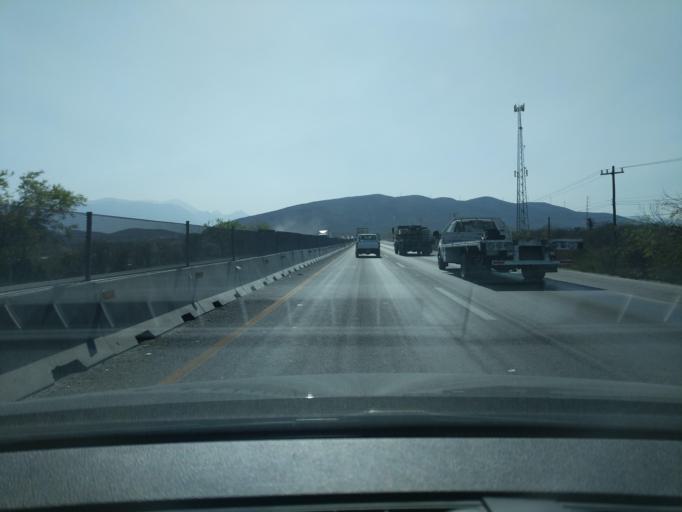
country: MX
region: Nuevo Leon
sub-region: Garcia
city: Los Parques
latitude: 25.7679
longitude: -100.4842
